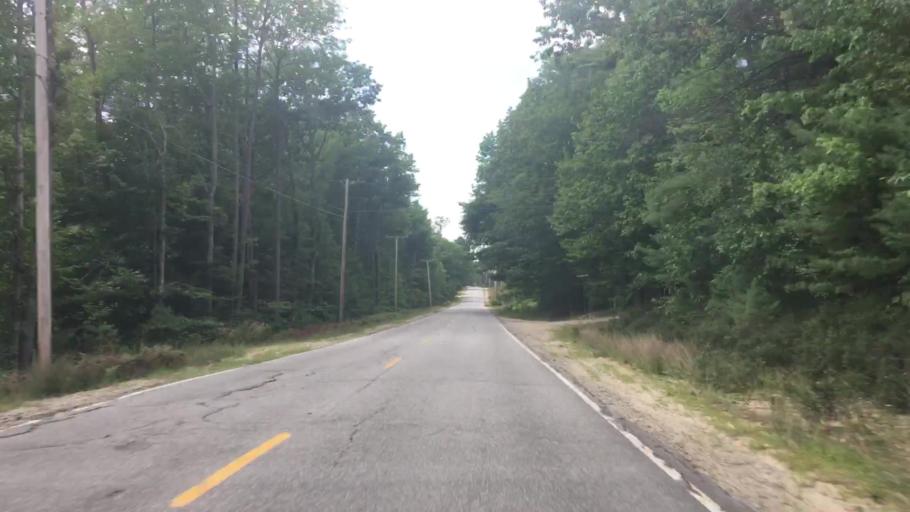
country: US
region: Maine
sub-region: Oxford County
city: Oxford
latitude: 44.0486
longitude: -70.5479
